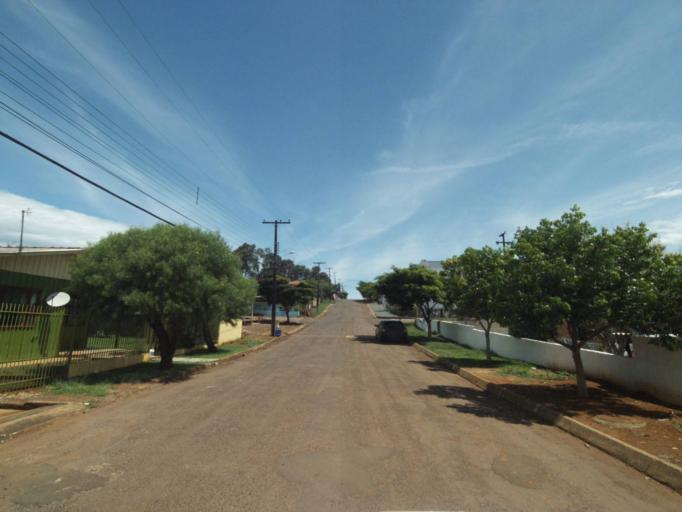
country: BR
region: Parana
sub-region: Guaraniacu
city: Guaraniacu
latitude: -25.0936
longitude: -52.8742
